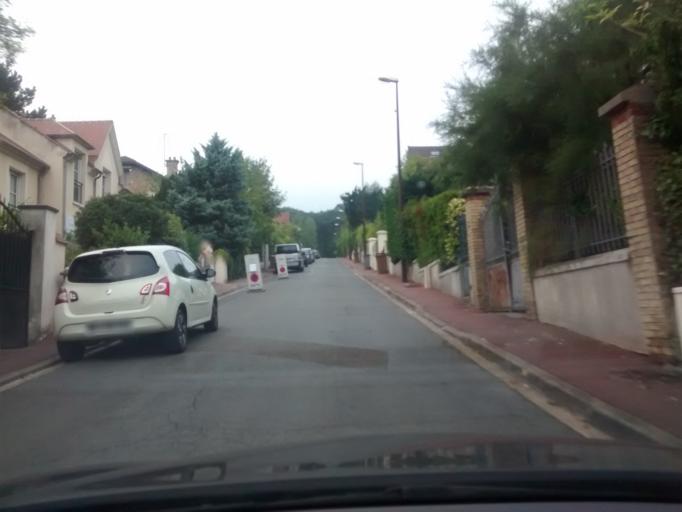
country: FR
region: Ile-de-France
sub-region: Departement des Hauts-de-Seine
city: Chaville
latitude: 48.8077
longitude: 2.1786
